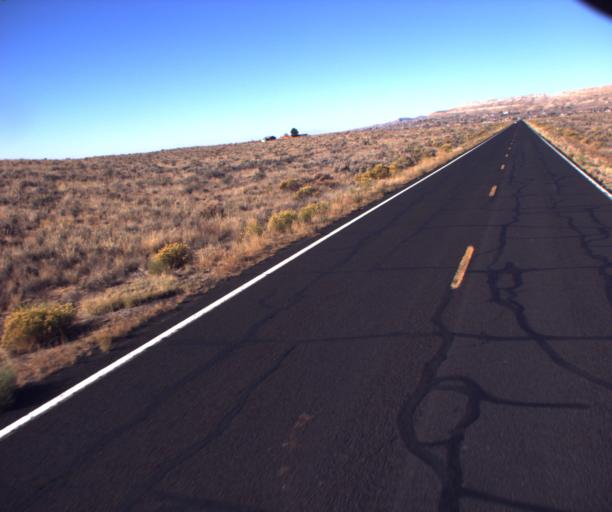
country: US
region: Arizona
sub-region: Navajo County
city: First Mesa
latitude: 35.8414
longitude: -110.3344
